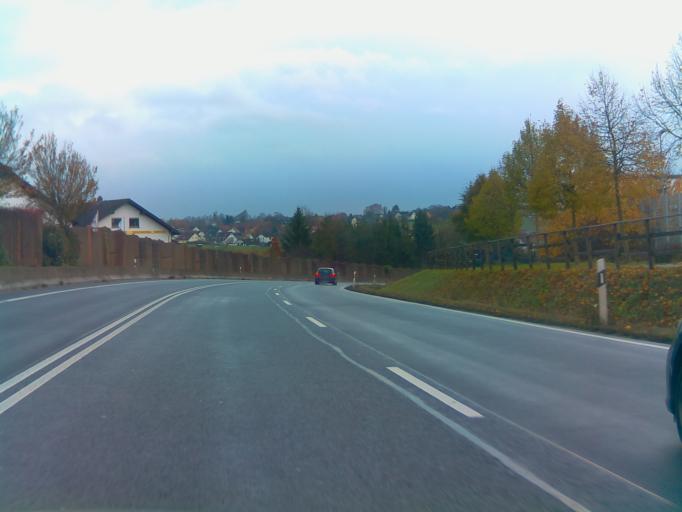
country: DE
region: Hesse
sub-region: Regierungsbezirk Kassel
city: Kunzell
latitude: 50.5377
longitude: 9.6989
